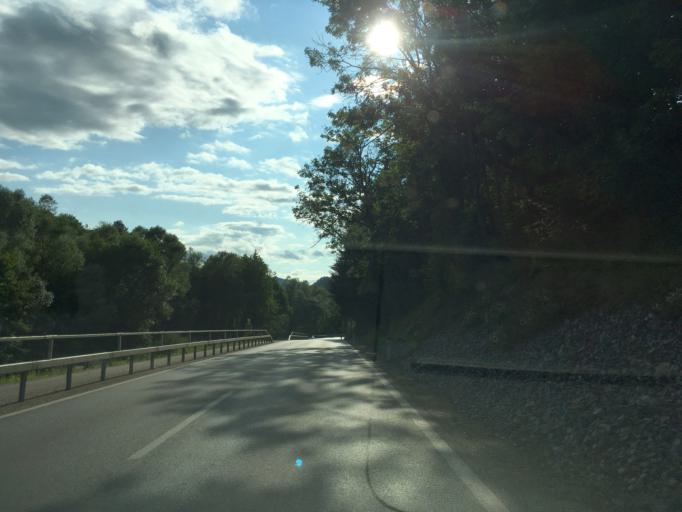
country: AT
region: Styria
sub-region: Politischer Bezirk Murau
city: Murau
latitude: 47.1136
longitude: 14.1587
